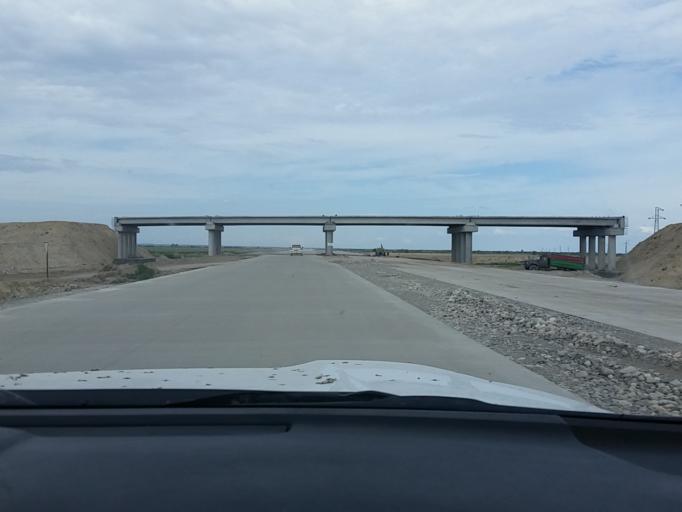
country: KZ
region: Almaty Oblysy
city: Zharkent
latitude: 44.0295
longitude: 79.9069
